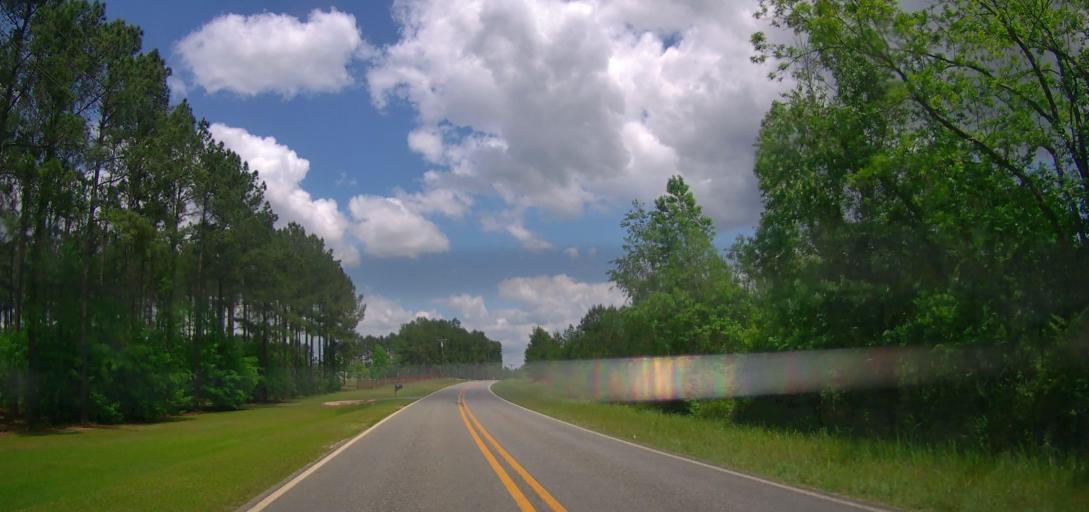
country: US
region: Georgia
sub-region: Laurens County
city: East Dublin
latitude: 32.5775
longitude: -82.7961
